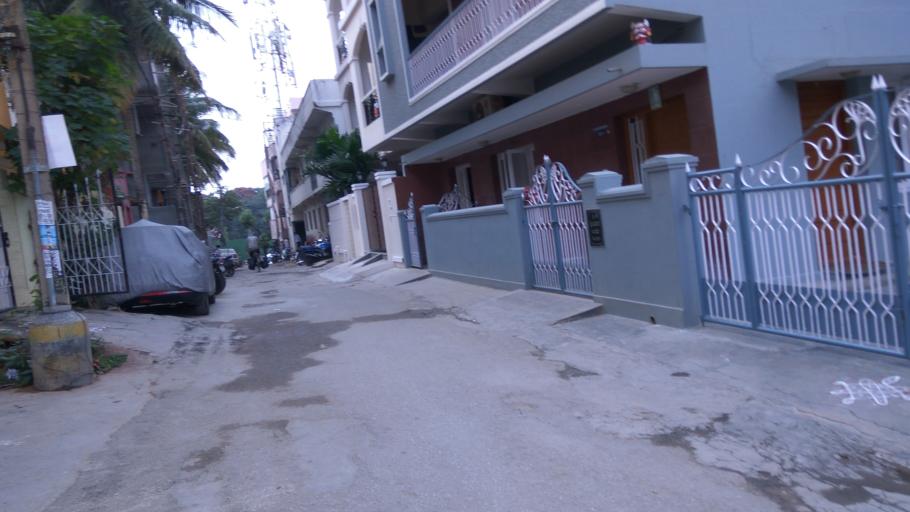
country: IN
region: Karnataka
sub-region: Bangalore Urban
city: Bangalore
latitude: 12.9733
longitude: 77.6380
